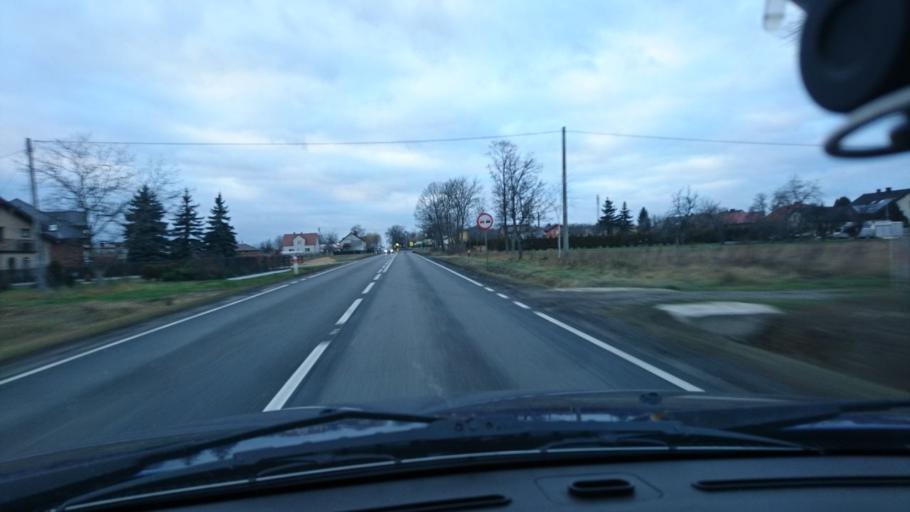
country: PL
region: Greater Poland Voivodeship
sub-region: Powiat kepinski
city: Slupia pod Kepnem
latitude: 51.2377
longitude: 18.0457
